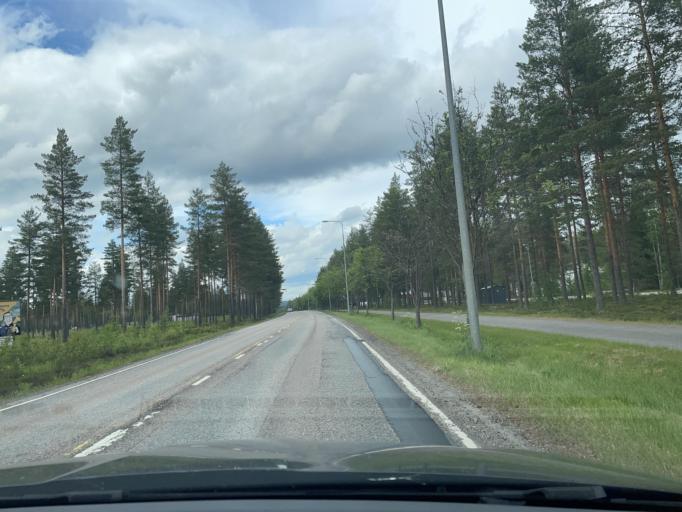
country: FI
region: Central Finland
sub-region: Jaemsae
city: Jaemsaenkoski
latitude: 61.9116
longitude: 25.1423
